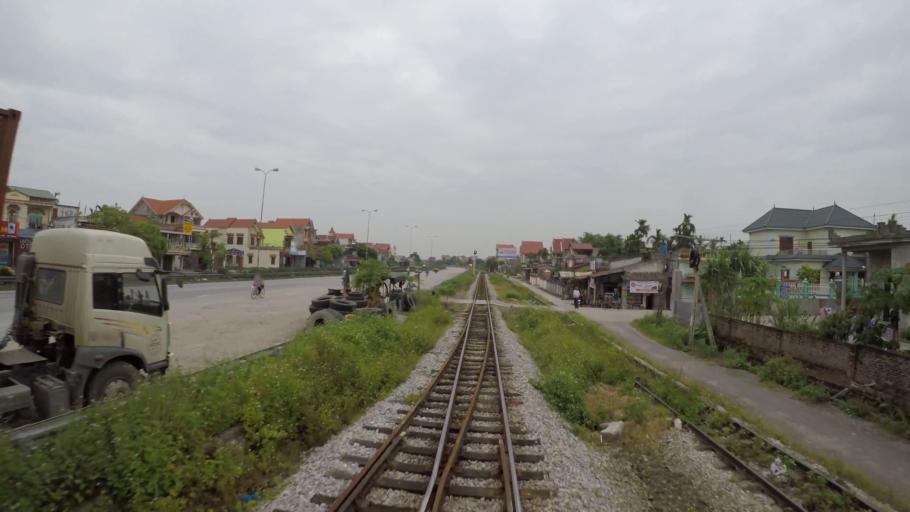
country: VN
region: Hai Duong
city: Phu Thai
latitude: 20.9727
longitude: 106.4396
